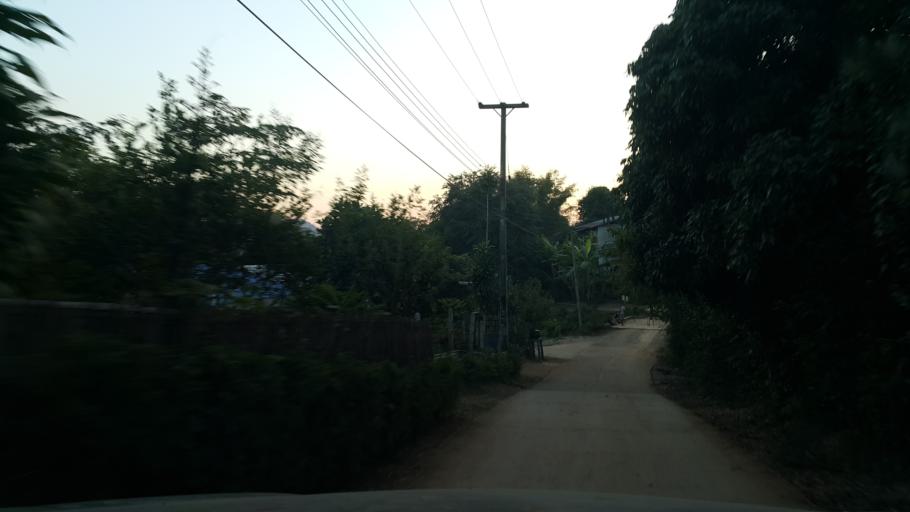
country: TH
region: Phrae
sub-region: Amphoe Wang Chin
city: Wang Chin
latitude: 17.8767
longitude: 99.6230
